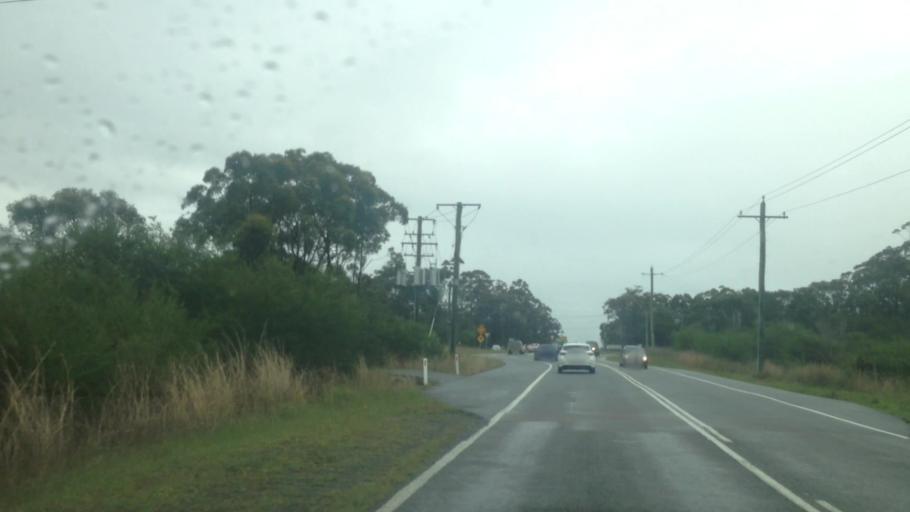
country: AU
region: New South Wales
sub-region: Wyong Shire
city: Charmhaven
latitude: -33.1580
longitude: 151.4787
